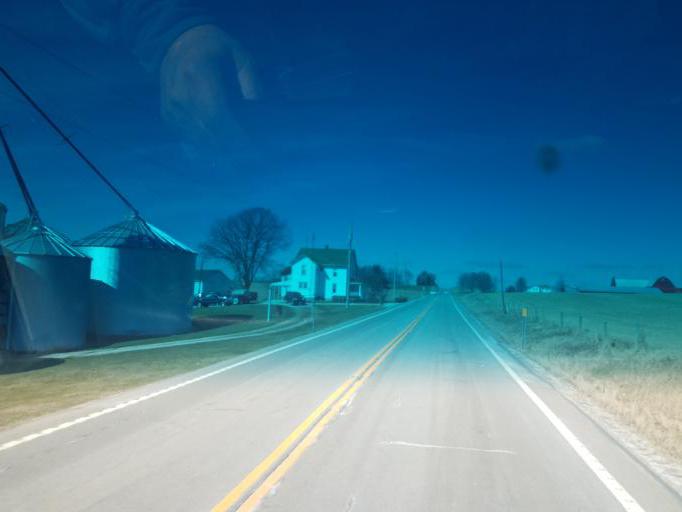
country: US
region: Ohio
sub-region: Ashland County
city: Loudonville
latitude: 40.7260
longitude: -82.2409
